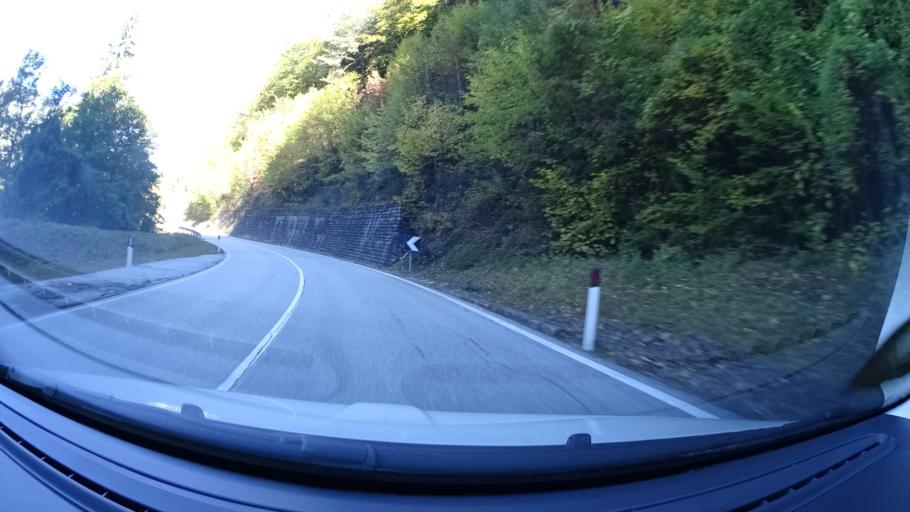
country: IT
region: Trentino-Alto Adige
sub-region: Provincia di Trento
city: Valda
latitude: 46.1994
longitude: 11.2738
